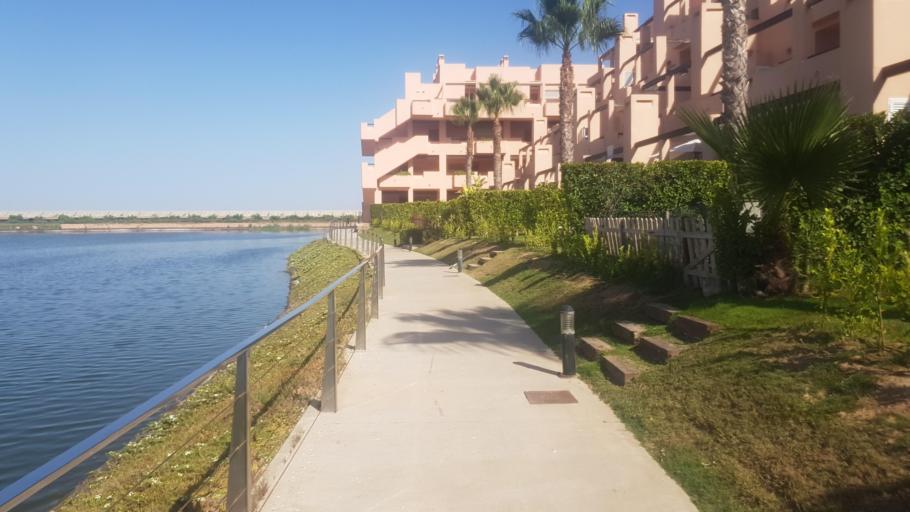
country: ES
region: Murcia
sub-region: Murcia
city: Mazarron
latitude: 37.7312
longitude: -1.3454
